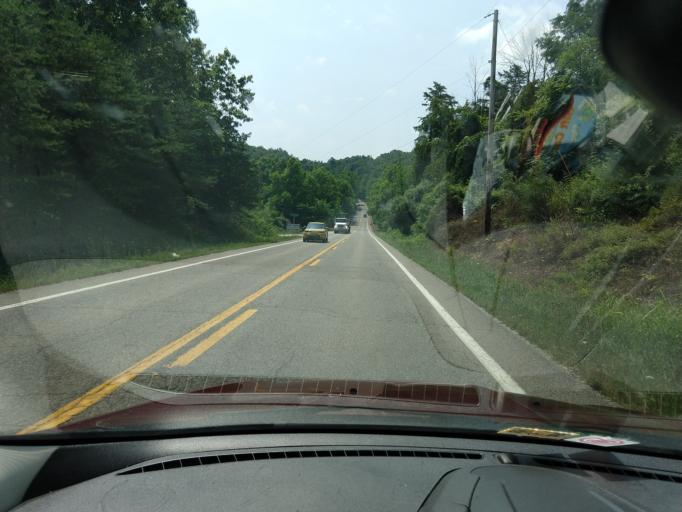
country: US
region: West Virginia
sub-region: Jackson County
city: Ripley
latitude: 38.8451
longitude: -81.7976
